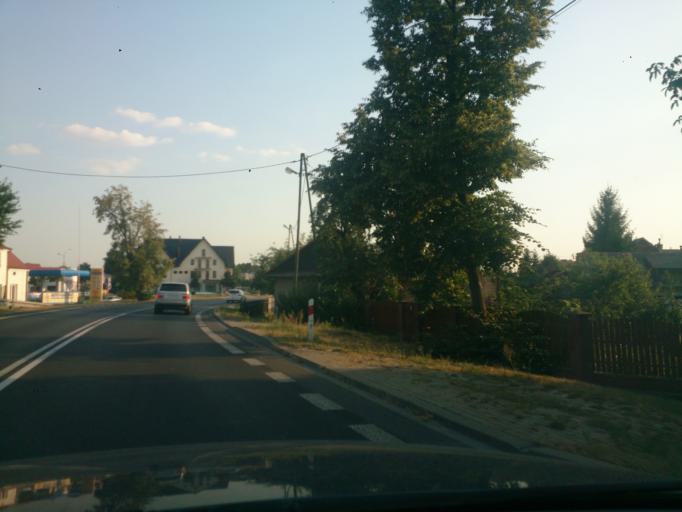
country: PL
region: Subcarpathian Voivodeship
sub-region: Powiat tarnobrzeski
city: Nowa Deba
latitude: 50.4310
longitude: 21.7512
